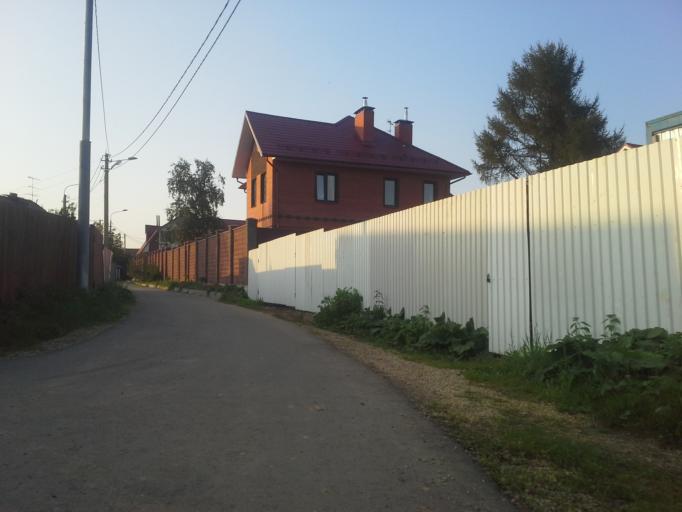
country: RU
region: Moskovskaya
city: Dubrovitsy
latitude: 55.5048
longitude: 37.4392
